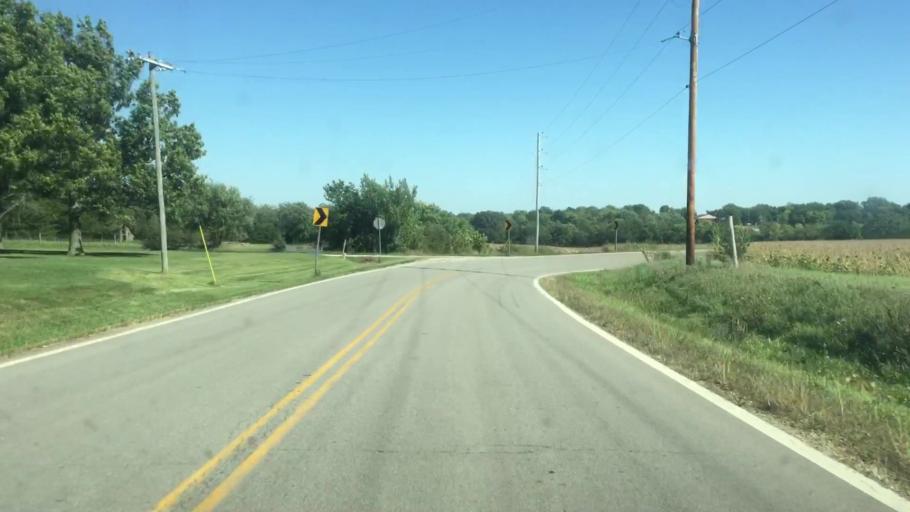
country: US
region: Kansas
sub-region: Brown County
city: Horton
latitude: 39.5949
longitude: -95.6214
